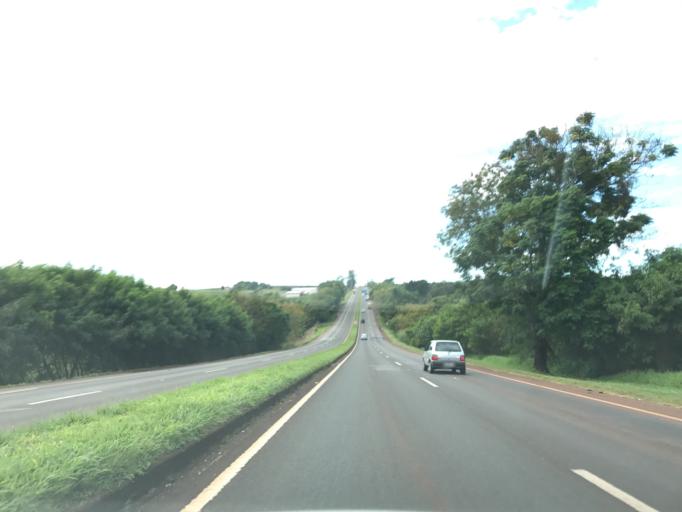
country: BR
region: Parana
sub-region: Marialva
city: Marialva
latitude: -23.5026
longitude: -51.7534
